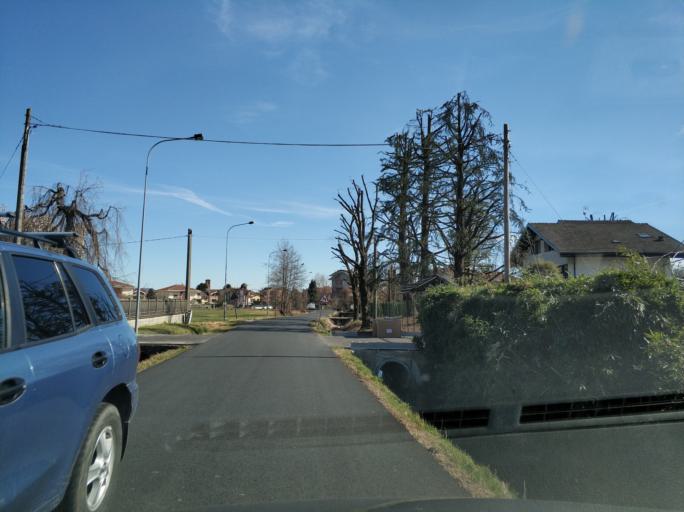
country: IT
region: Piedmont
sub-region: Provincia di Torino
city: Leini
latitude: 45.1875
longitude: 7.7055
